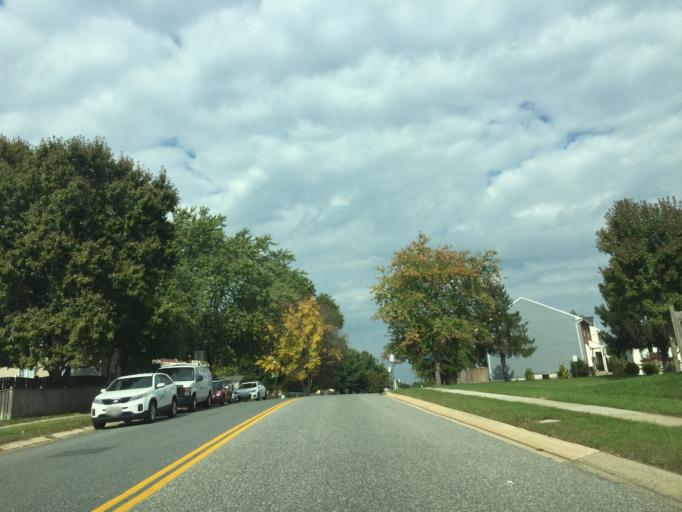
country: US
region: Maryland
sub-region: Harford County
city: Bel Air South
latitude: 39.4773
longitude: -76.3073
